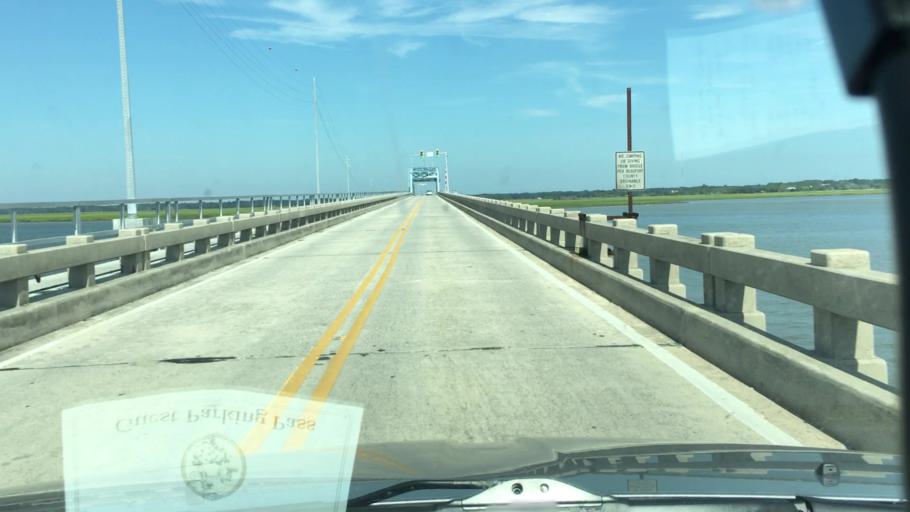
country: US
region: South Carolina
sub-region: Beaufort County
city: Beaufort
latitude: 32.4034
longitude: -80.4506
